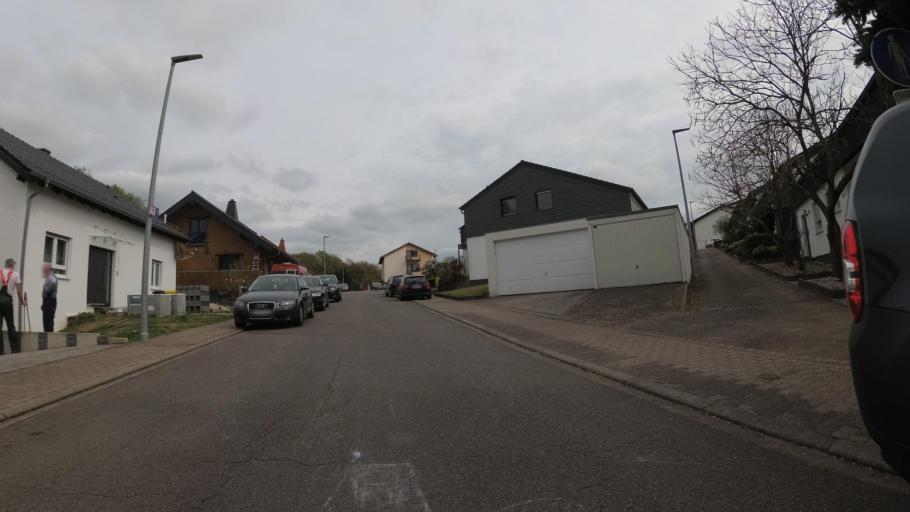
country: DE
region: Rheinland-Pfalz
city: Zweibrucken
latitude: 49.2501
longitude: 7.3862
